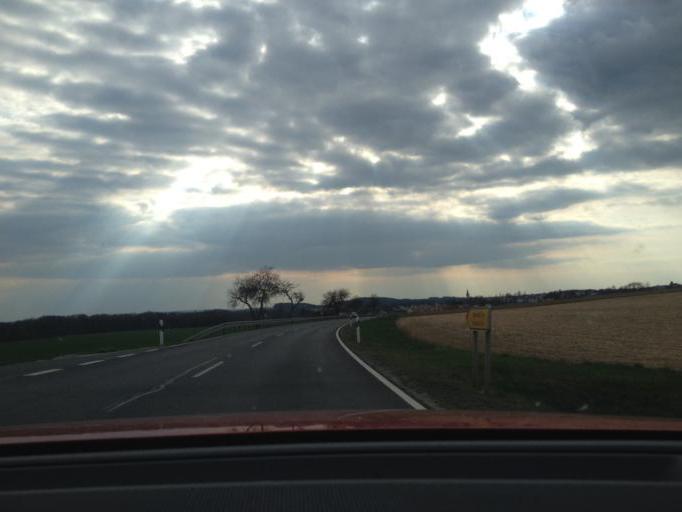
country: DE
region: Bavaria
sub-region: Upper Palatinate
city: Kulmain
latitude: 49.8971
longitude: 11.9202
